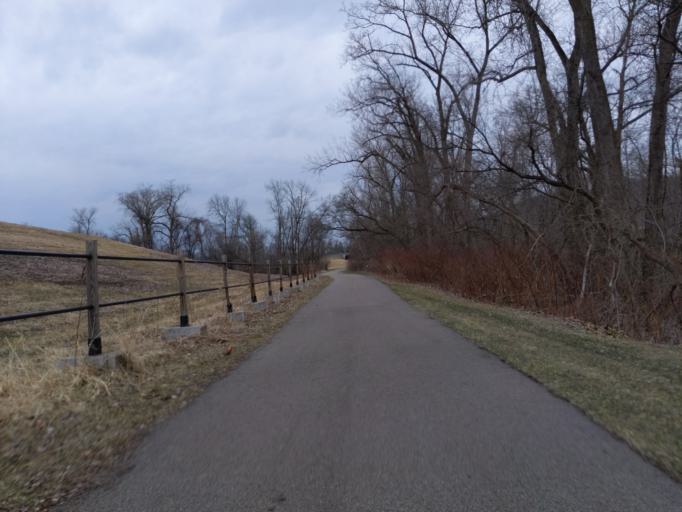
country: US
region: New York
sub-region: Chemung County
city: Elmira
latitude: 42.0937
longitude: -76.7866
